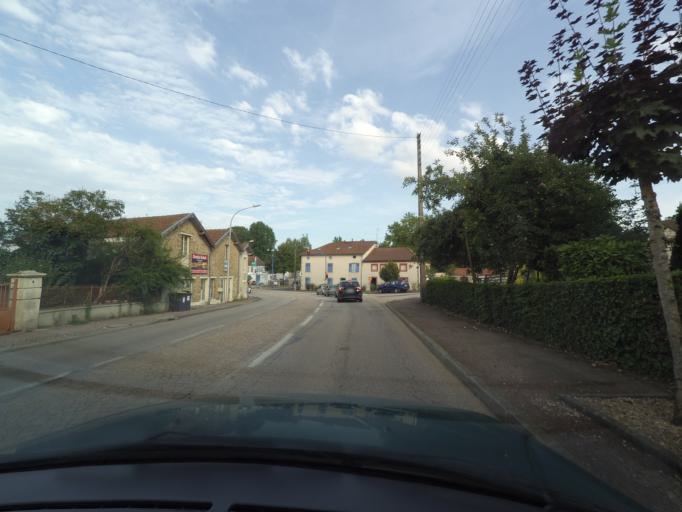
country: FR
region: Limousin
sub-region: Departement de la Haute-Vienne
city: Aixe-sur-Vienne
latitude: 45.7953
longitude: 1.1256
